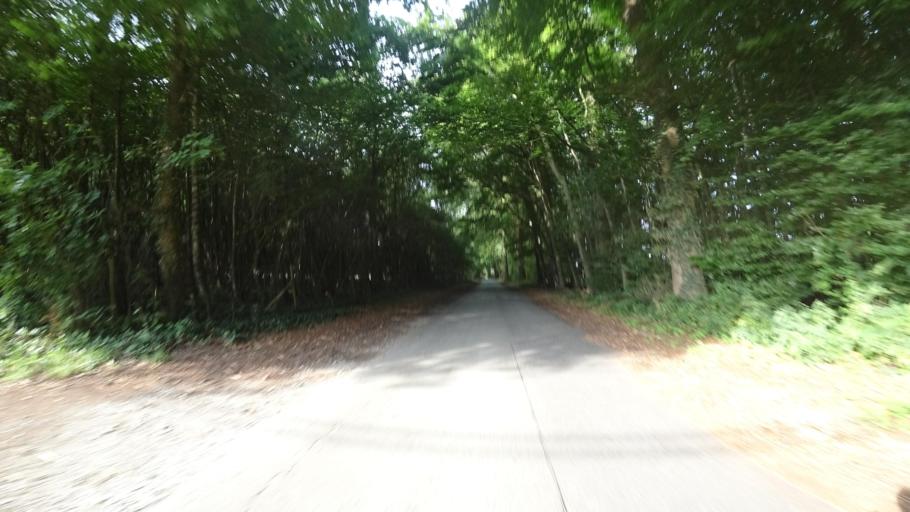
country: DE
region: North Rhine-Westphalia
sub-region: Regierungsbezirk Detmold
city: Steinhagen
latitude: 51.9524
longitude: 8.4254
